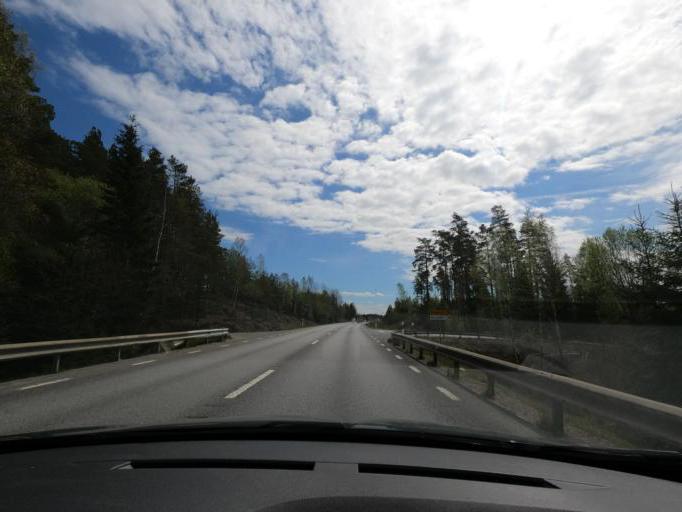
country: SE
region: Joenkoeping
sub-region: Gislaveds Kommun
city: Gislaved
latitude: 57.3263
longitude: 13.5389
